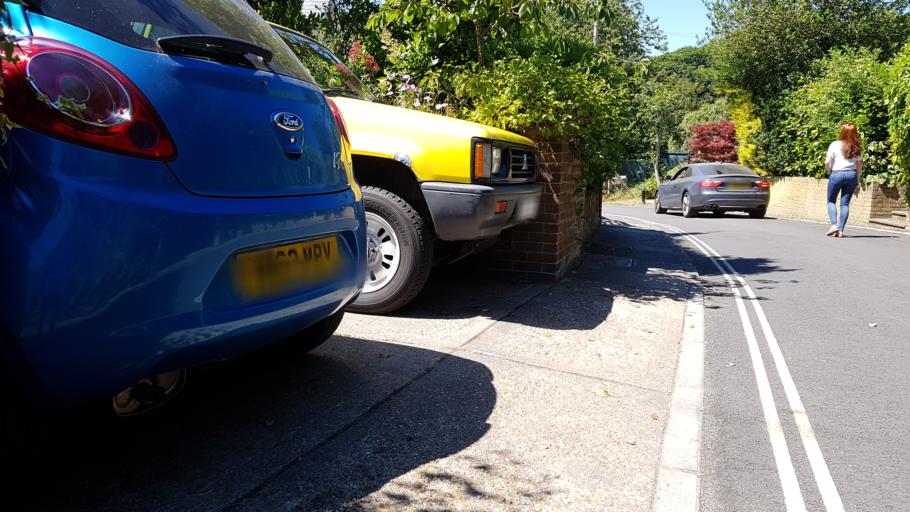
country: GB
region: England
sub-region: Isle of Wight
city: Newport
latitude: 50.6908
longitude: -1.3097
